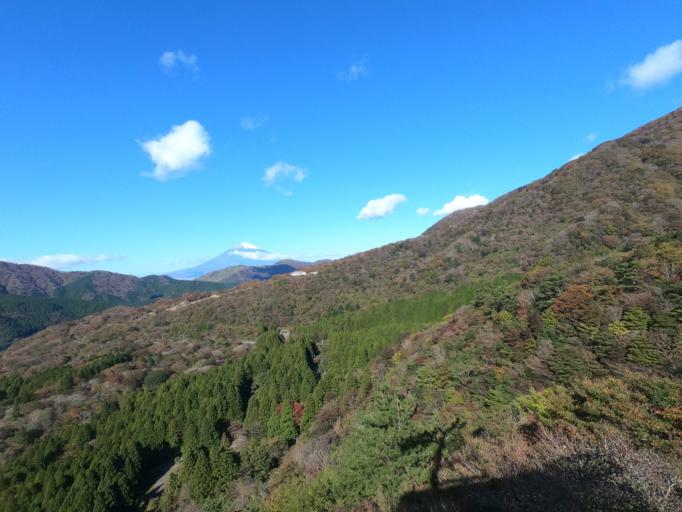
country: JP
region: Kanagawa
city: Hakone
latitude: 35.2164
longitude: 139.0142
